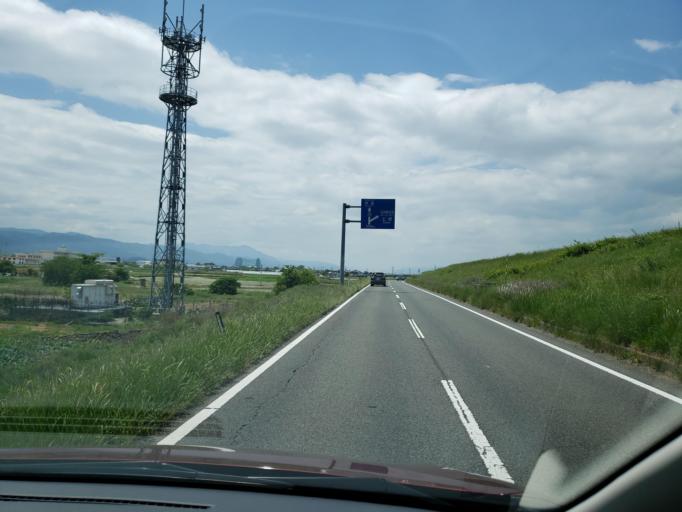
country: JP
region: Tokushima
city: Ishii
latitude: 34.1009
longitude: 134.4452
